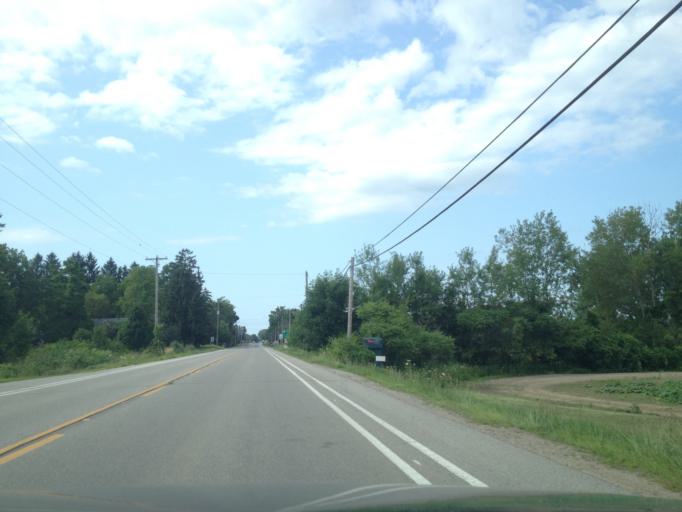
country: CA
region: Ontario
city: Aylmer
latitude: 42.6716
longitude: -80.9856
